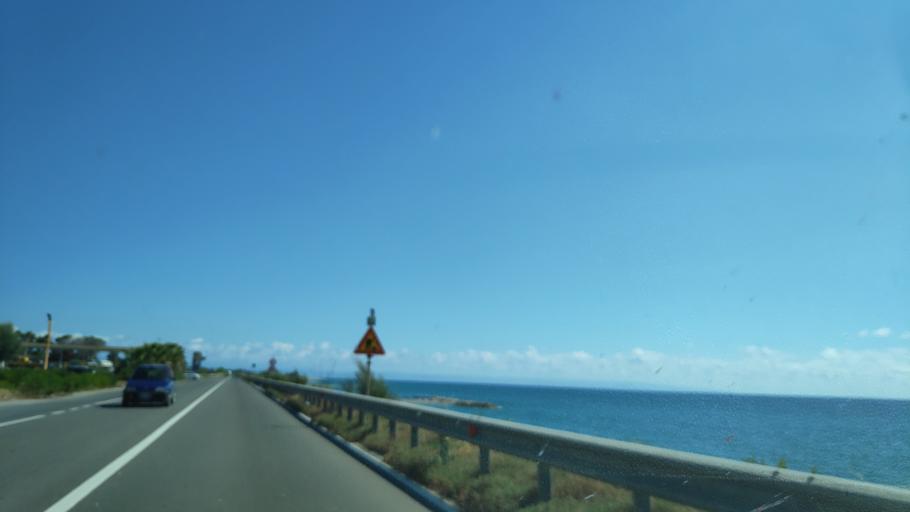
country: IT
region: Calabria
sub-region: Provincia di Cosenza
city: Campora San Giovanni
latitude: 39.0532
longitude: 16.0948
